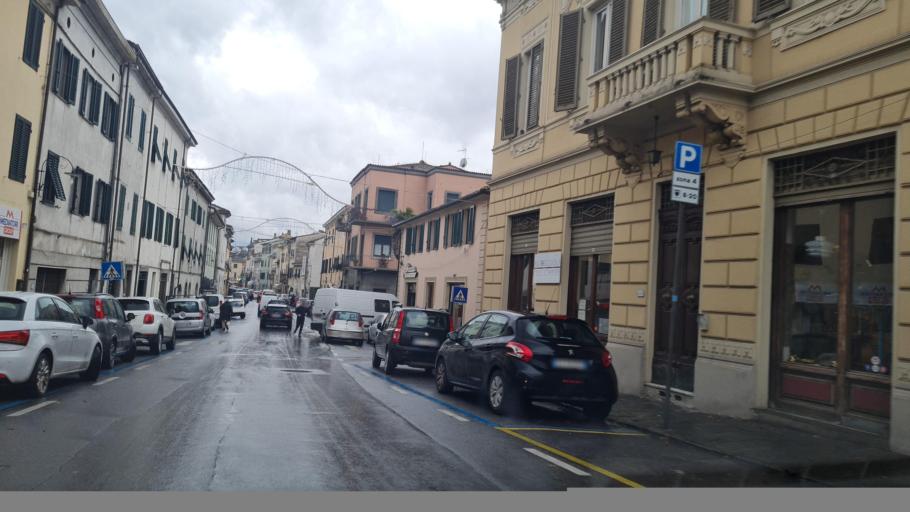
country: IT
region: Tuscany
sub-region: Provincia di Lucca
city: Lucca
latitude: 43.8548
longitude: 10.5078
